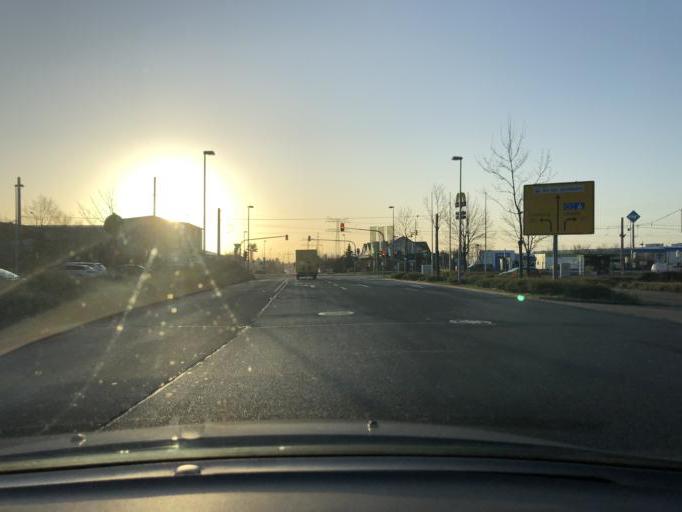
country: DE
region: Saxony
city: Taucha
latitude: 51.3734
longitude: 12.4753
